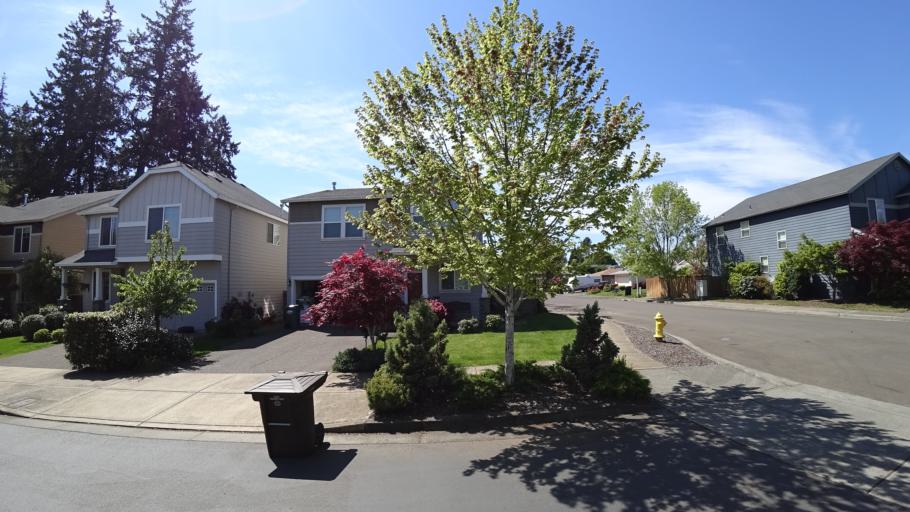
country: US
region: Oregon
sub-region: Washington County
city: Hillsboro
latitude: 45.5196
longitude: -122.9517
